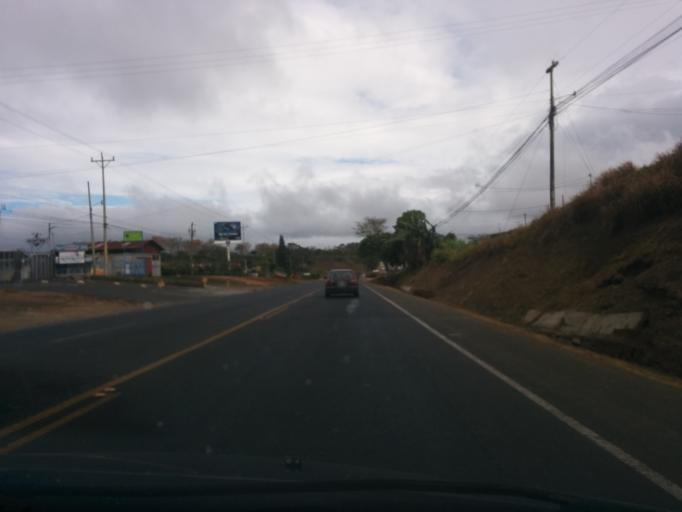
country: CR
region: Alajuela
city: San Rafael
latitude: 10.0698
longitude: -84.4553
